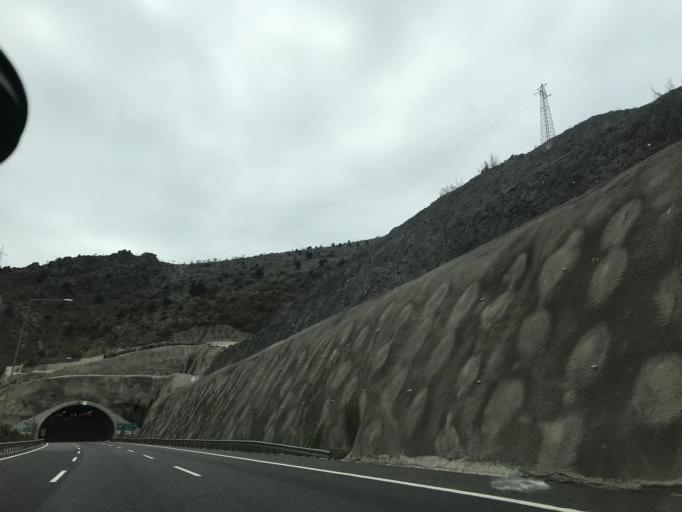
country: TR
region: Nigde
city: Ciftehan
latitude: 37.5485
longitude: 34.7828
